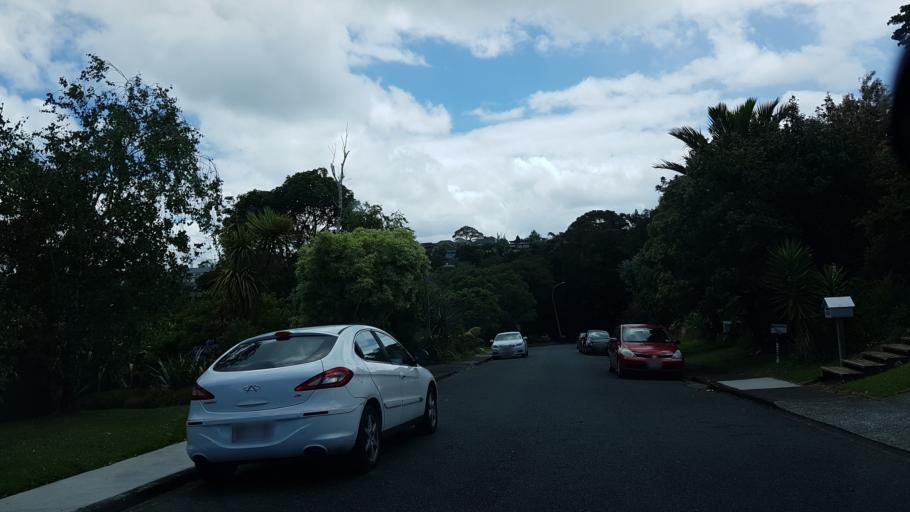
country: NZ
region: Auckland
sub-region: Auckland
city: North Shore
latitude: -36.8035
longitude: 174.7342
